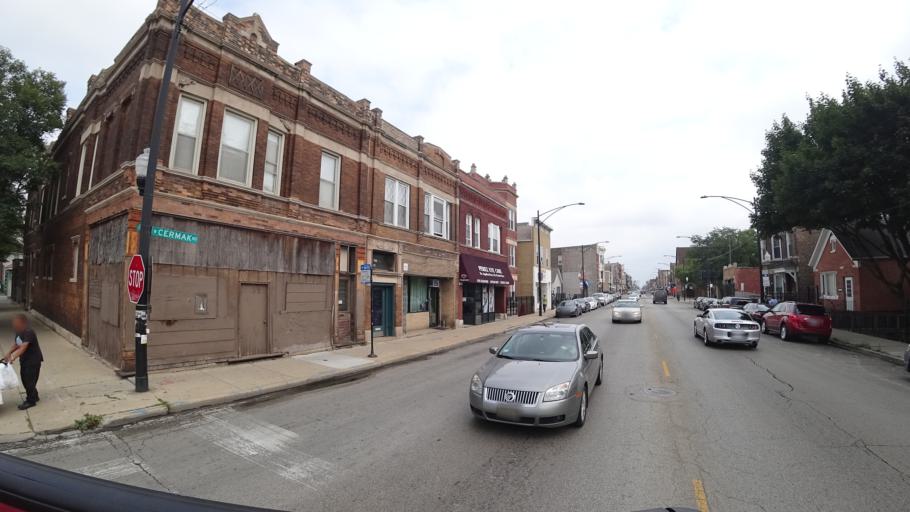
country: US
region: Illinois
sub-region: Cook County
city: Chicago
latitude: 41.8521
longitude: -87.6831
